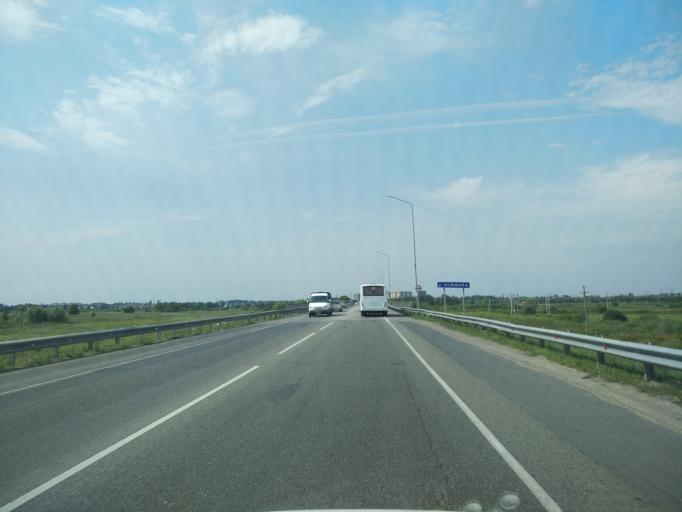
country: RU
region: Voronezj
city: Somovo
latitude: 51.6857
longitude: 39.3522
